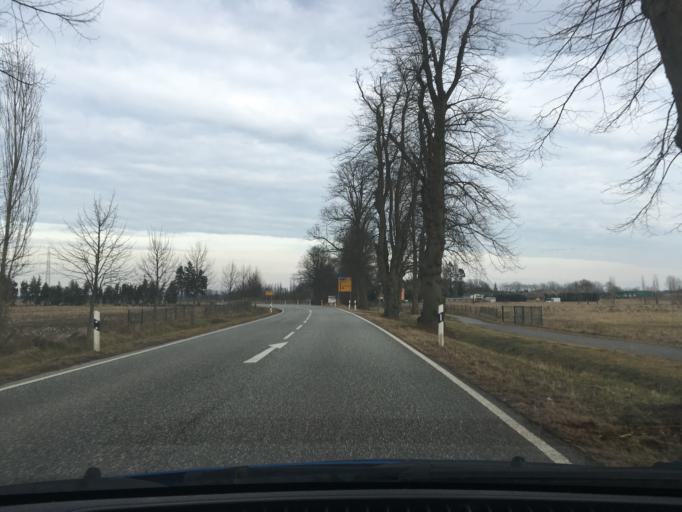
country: DE
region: Mecklenburg-Vorpommern
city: Wittenburg
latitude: 53.5189
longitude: 11.0418
